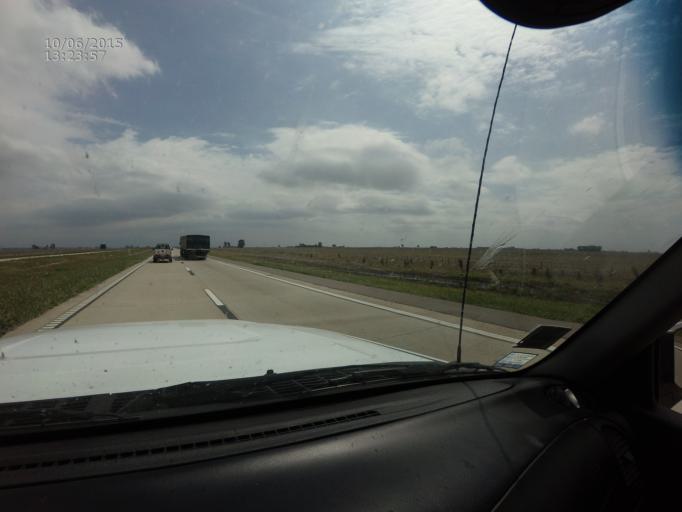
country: AR
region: Cordoba
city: Marcos Juarez
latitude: -32.6589
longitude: -62.1279
